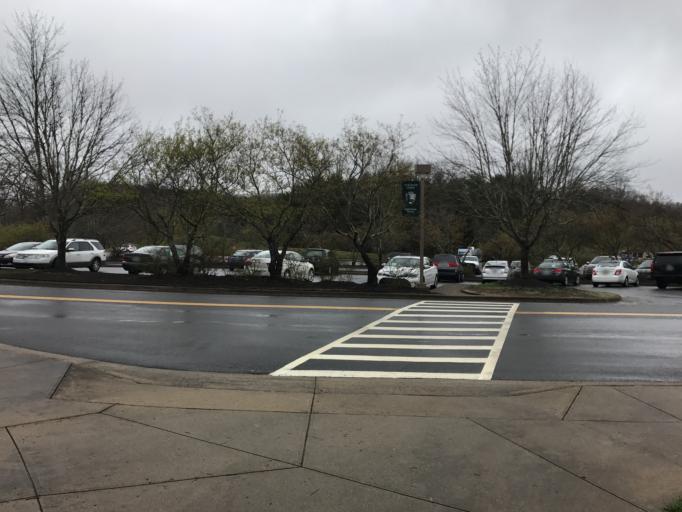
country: US
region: West Virginia
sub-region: Fayette County
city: Fayetteville
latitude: 38.0707
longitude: -81.0764
